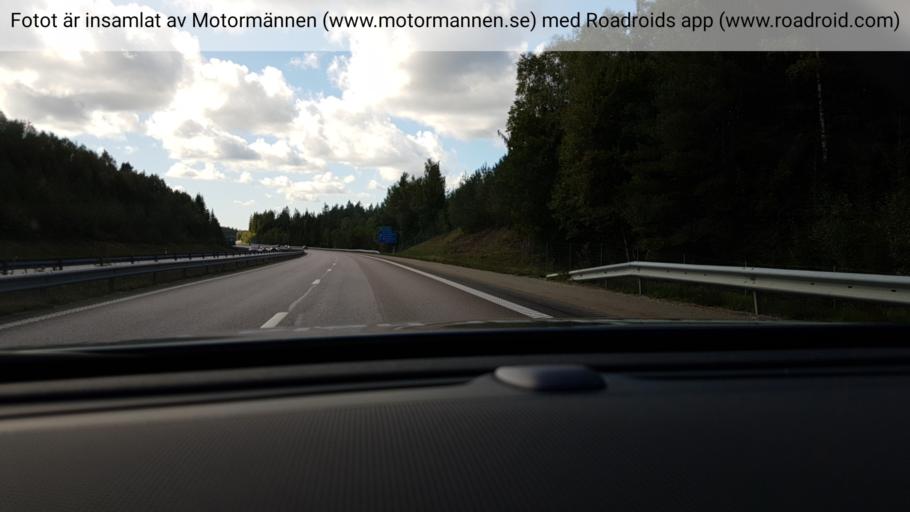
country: SE
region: Vaestra Goetaland
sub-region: Bollebygds Kommun
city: Bollebygd
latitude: 57.6710
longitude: 12.6217
